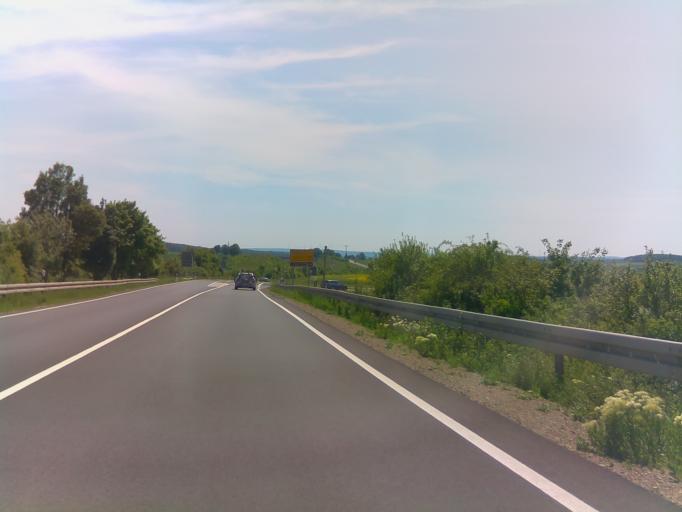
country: DE
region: Bavaria
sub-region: Regierungsbezirk Unterfranken
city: Oerlenbach
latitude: 50.1394
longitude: 10.1501
